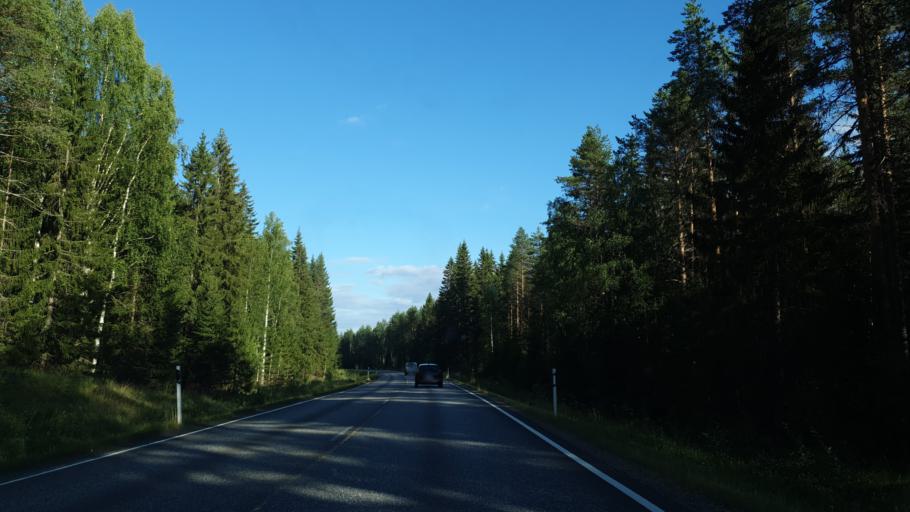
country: FI
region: North Karelia
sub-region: Joensuu
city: Outokumpu
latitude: 62.5221
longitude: 29.0040
